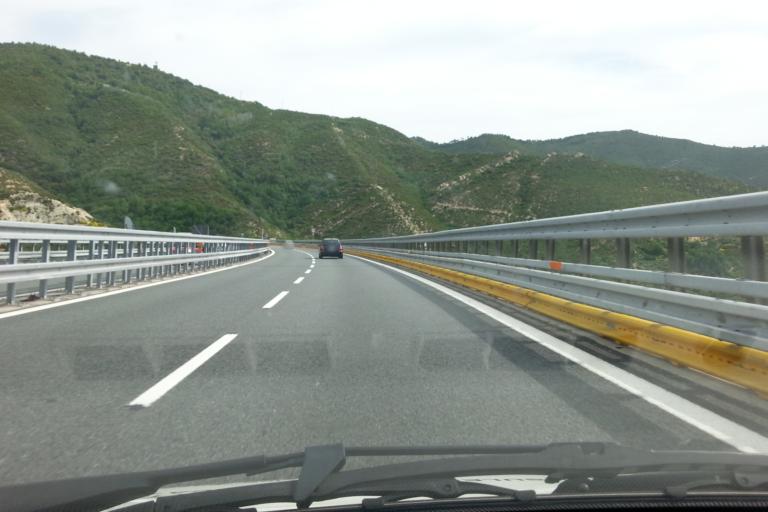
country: IT
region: Liguria
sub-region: Provincia di Savona
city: Spotorno
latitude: 44.2309
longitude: 8.3989
